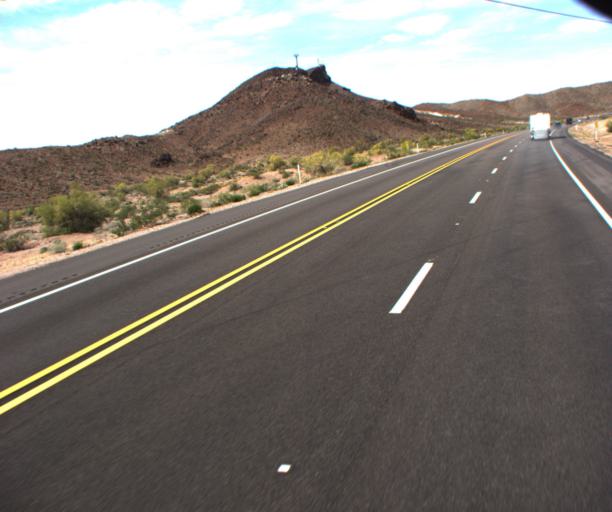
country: US
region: Arizona
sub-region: Mohave County
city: Desert Hills
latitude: 34.5937
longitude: -114.3694
